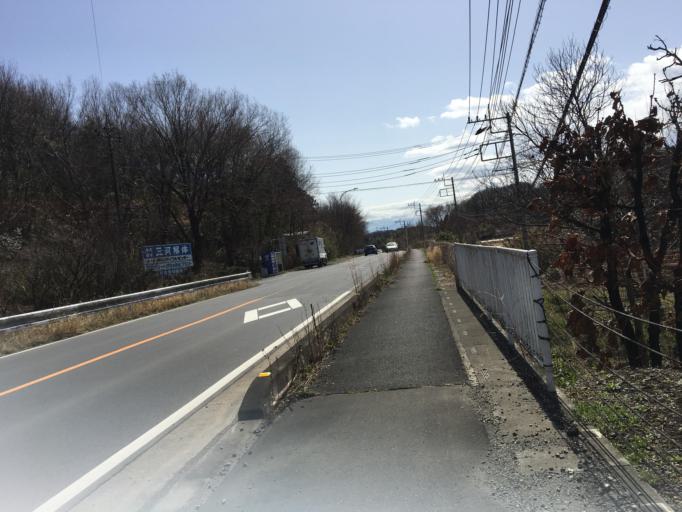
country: JP
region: Saitama
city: Sakado
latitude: 35.9972
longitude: 139.3340
